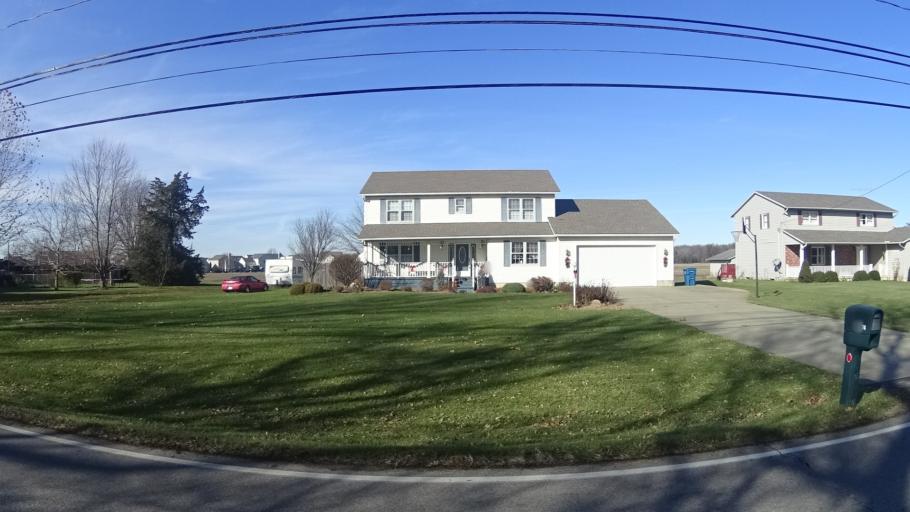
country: US
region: Ohio
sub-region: Lorain County
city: North Ridgeville
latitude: 41.3534
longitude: -82.0335
